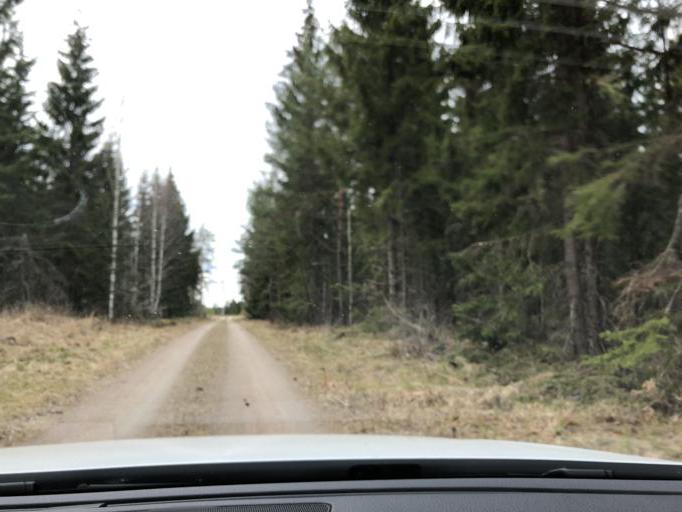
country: SE
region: Gaevleborg
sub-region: Gavle Kommun
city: Hedesunda
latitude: 60.3431
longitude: 17.0964
